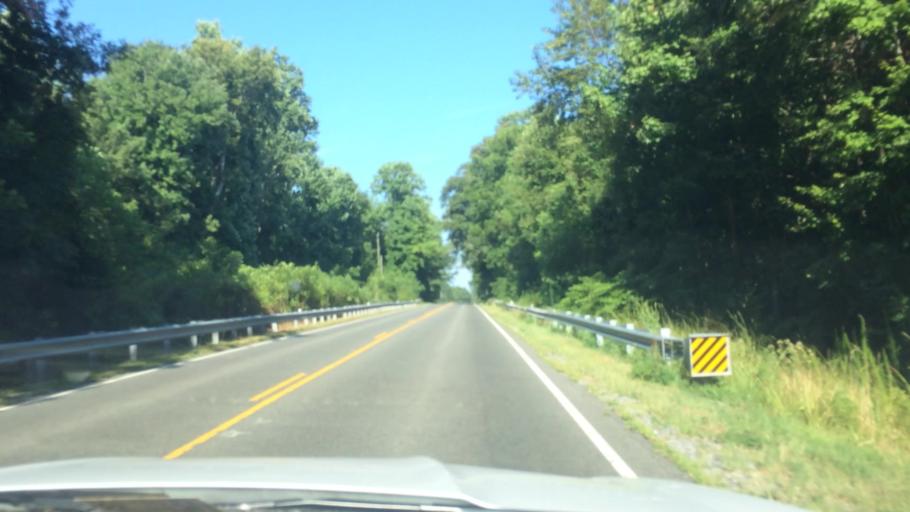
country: US
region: Virginia
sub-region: Lancaster County
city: Lancaster
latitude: 37.7691
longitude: -76.4954
